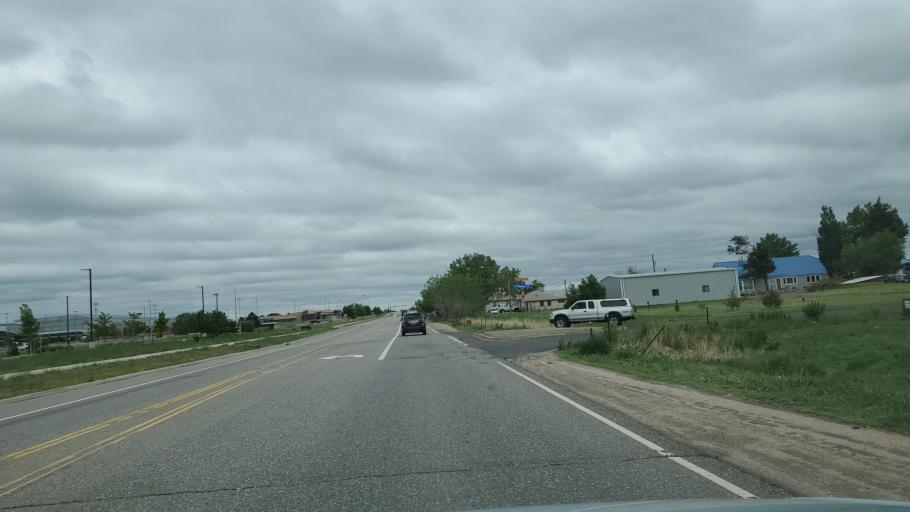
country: US
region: Colorado
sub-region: Adams County
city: Todd Creek
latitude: 39.9144
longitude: -104.8438
